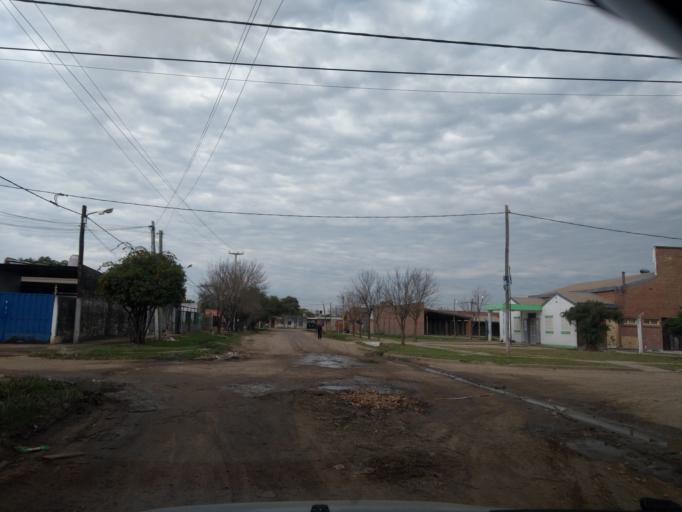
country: AR
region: Chaco
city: Resistencia
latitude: -27.4800
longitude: -58.9795
